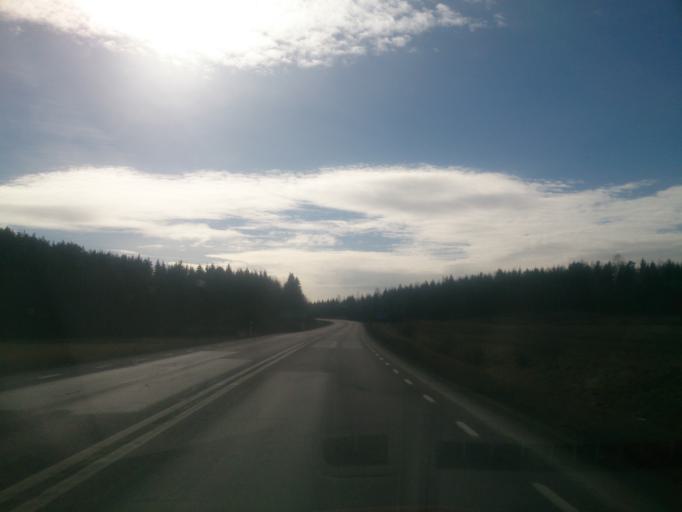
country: SE
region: OEstergoetland
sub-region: Norrkopings Kommun
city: Kimstad
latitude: 58.5372
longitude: 15.9772
